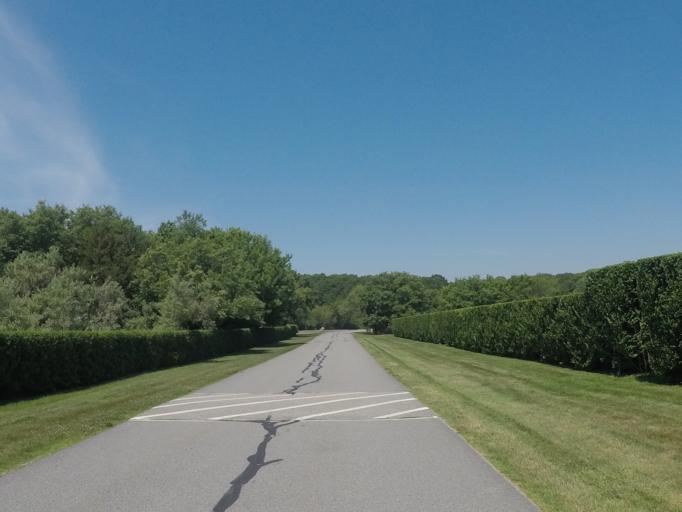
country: US
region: Massachusetts
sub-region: Bristol County
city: Bliss Corner
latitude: 41.5450
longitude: -70.9406
